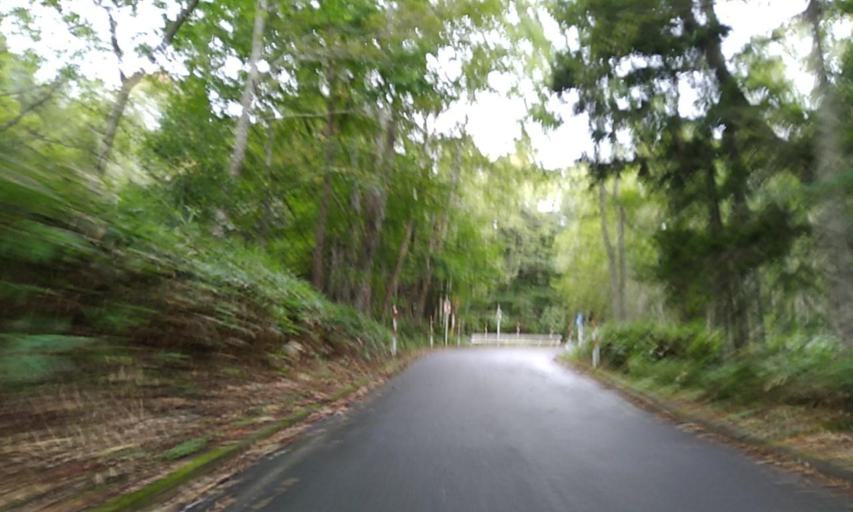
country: JP
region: Hokkaido
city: Bihoro
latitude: 43.5808
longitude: 144.2592
